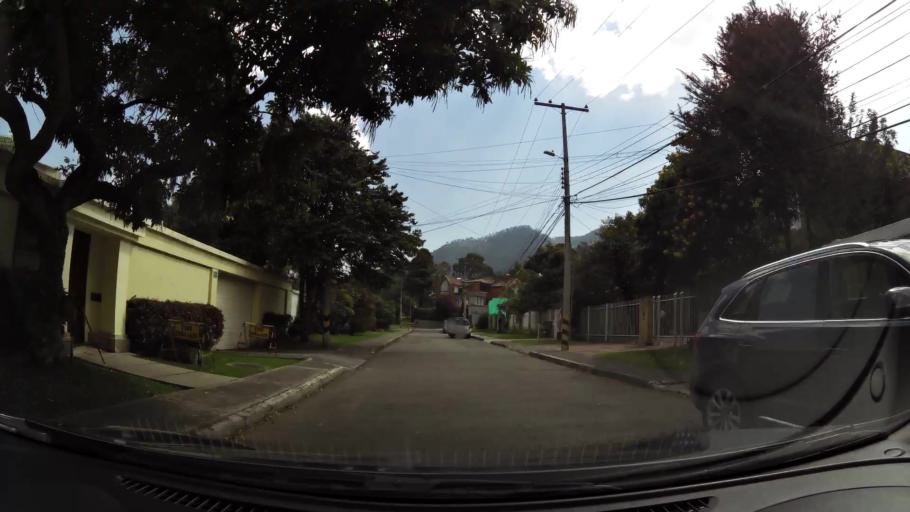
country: CO
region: Bogota D.C.
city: Barrio San Luis
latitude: 4.6857
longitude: -74.0317
